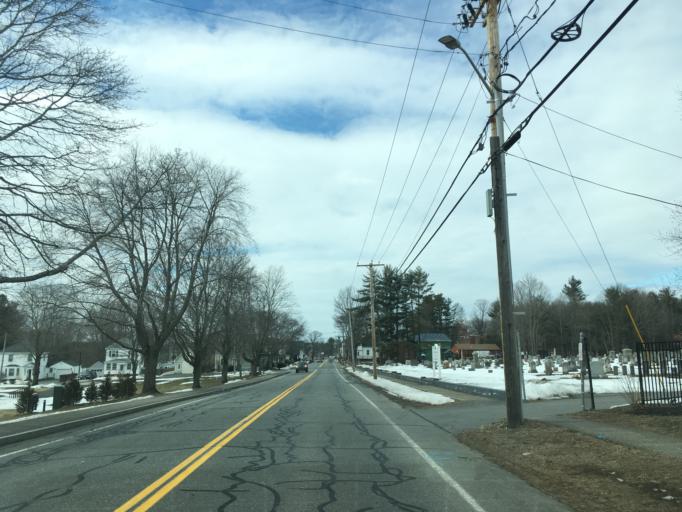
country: US
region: New Hampshire
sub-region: Rockingham County
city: Hampton
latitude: 42.9399
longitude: -70.8317
